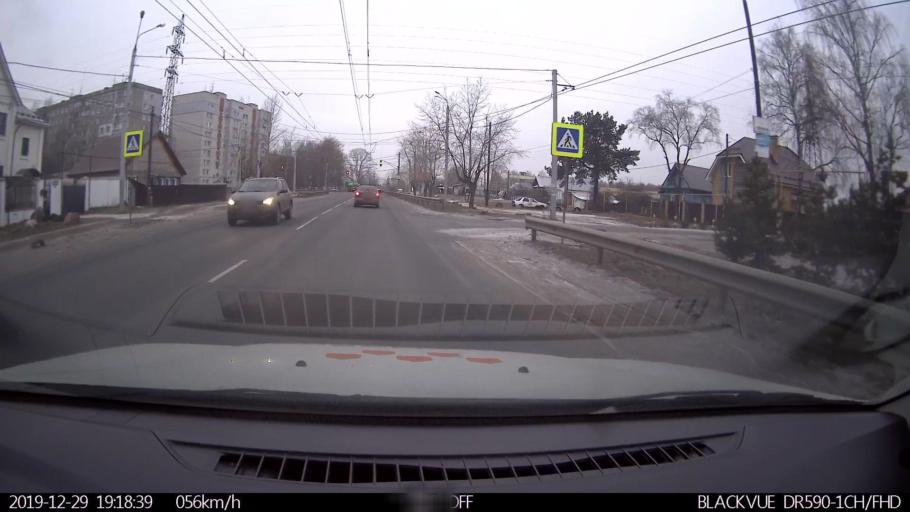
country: RU
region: Nizjnij Novgorod
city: Gorbatovka
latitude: 56.3815
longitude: 43.8007
